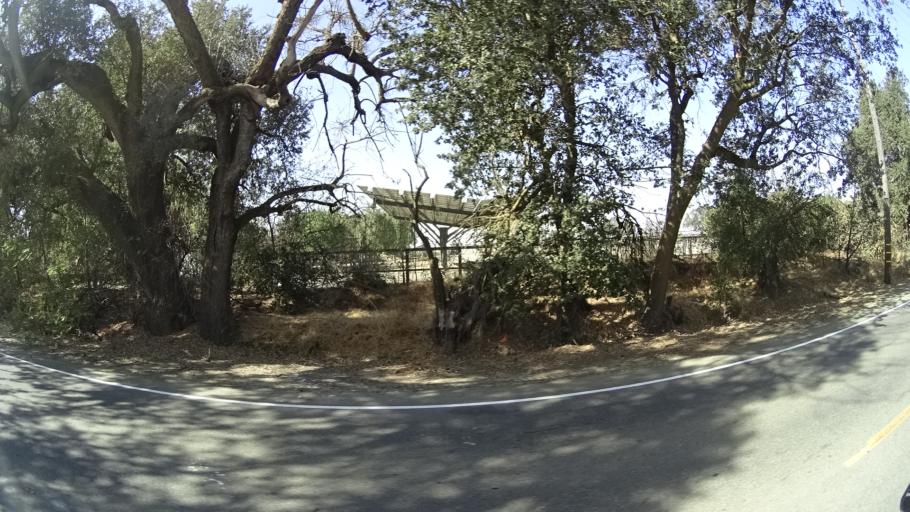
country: US
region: California
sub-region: Yolo County
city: Davis
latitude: 38.5299
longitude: -121.6946
